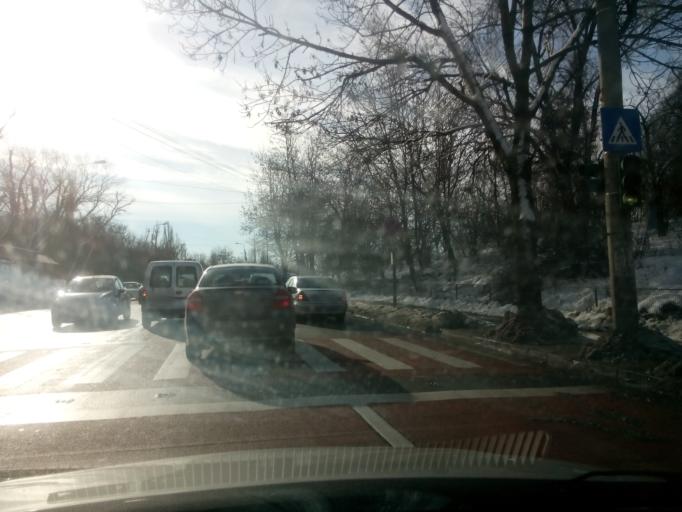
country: RO
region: Ilfov
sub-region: Comuna Popesti-Leordeni
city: Popesti-Leordeni
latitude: 44.3918
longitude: 26.1425
